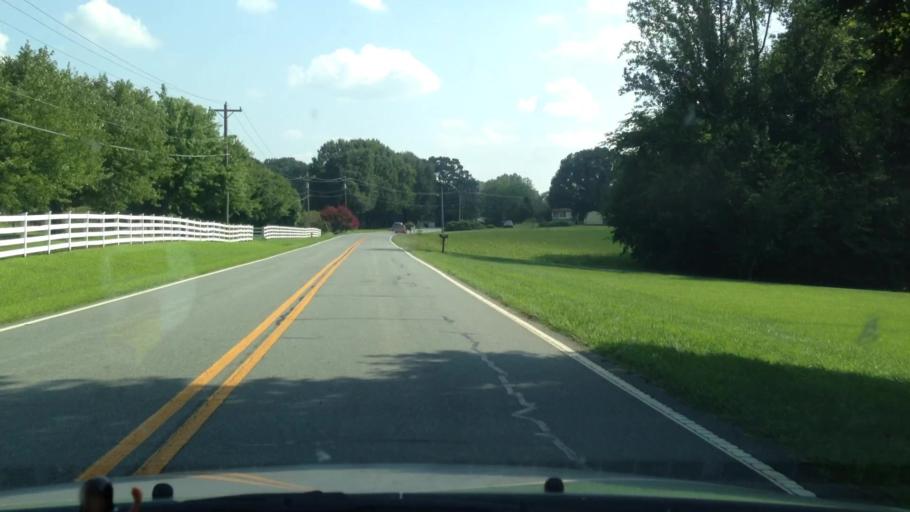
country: US
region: North Carolina
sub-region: Guilford County
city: Oak Ridge
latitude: 36.2095
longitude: -80.0552
